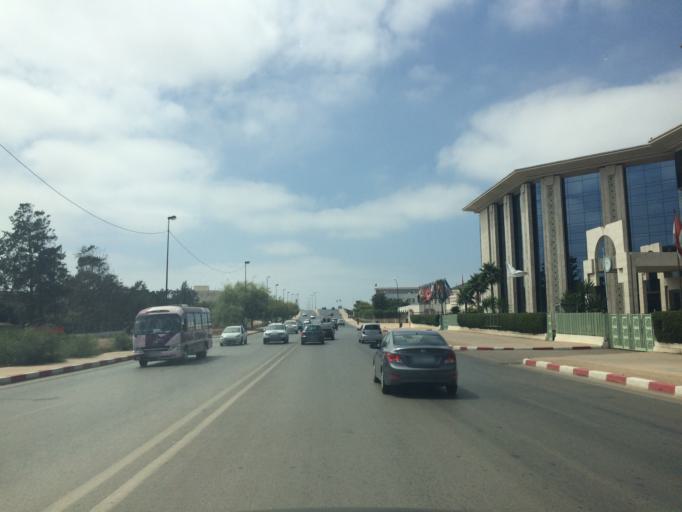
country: MA
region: Rabat-Sale-Zemmour-Zaer
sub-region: Skhirate-Temara
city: Temara
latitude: 33.9698
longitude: -6.8754
